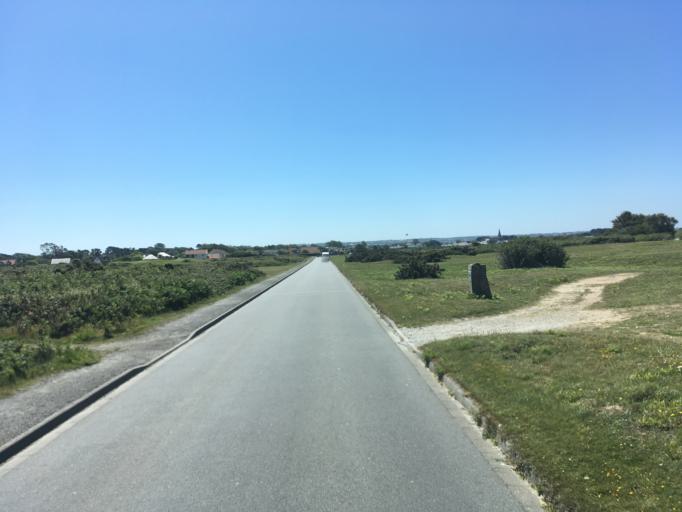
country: GG
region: St Peter Port
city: Saint Peter Port
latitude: 49.5026
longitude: -2.5331
